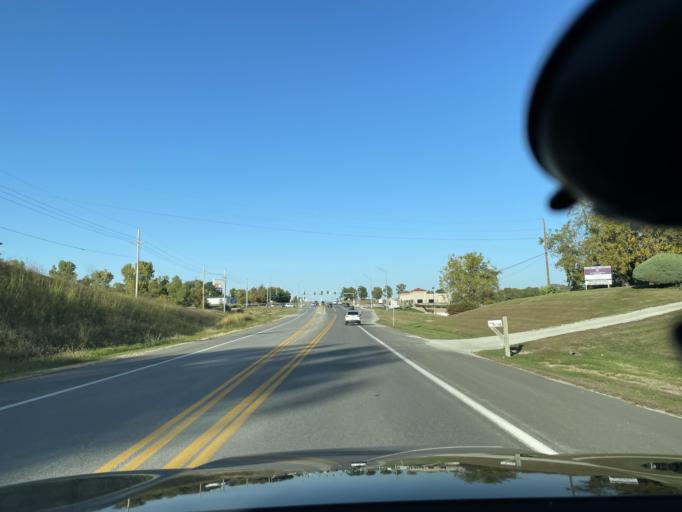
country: US
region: Missouri
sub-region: Andrew County
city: Country Club Village
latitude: 39.8102
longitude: -94.8082
